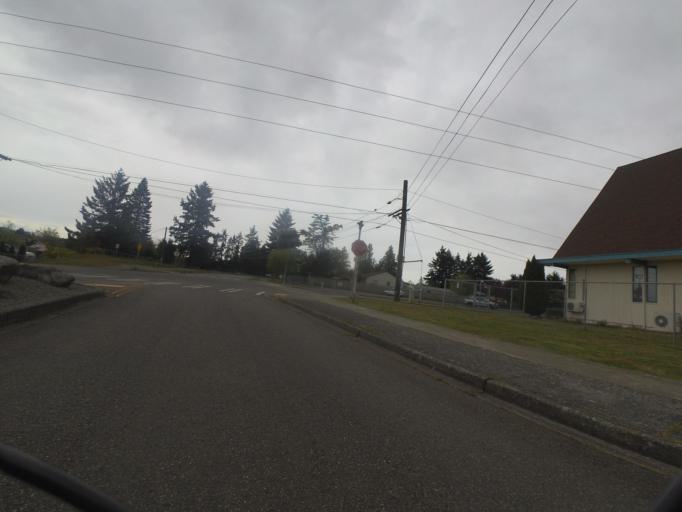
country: US
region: Washington
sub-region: Pierce County
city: Lakewood
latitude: 47.1971
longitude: -122.4760
